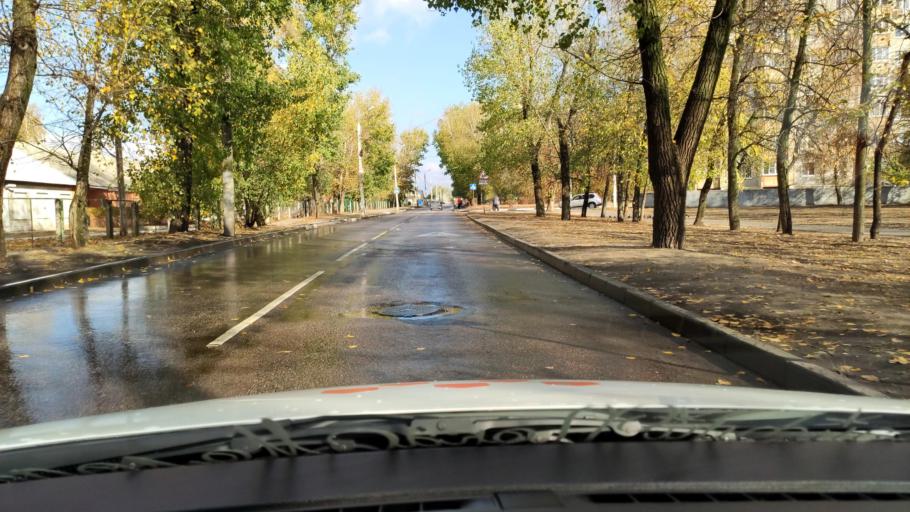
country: RU
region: Voronezj
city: Pridonskoy
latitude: 51.6845
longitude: 39.0775
